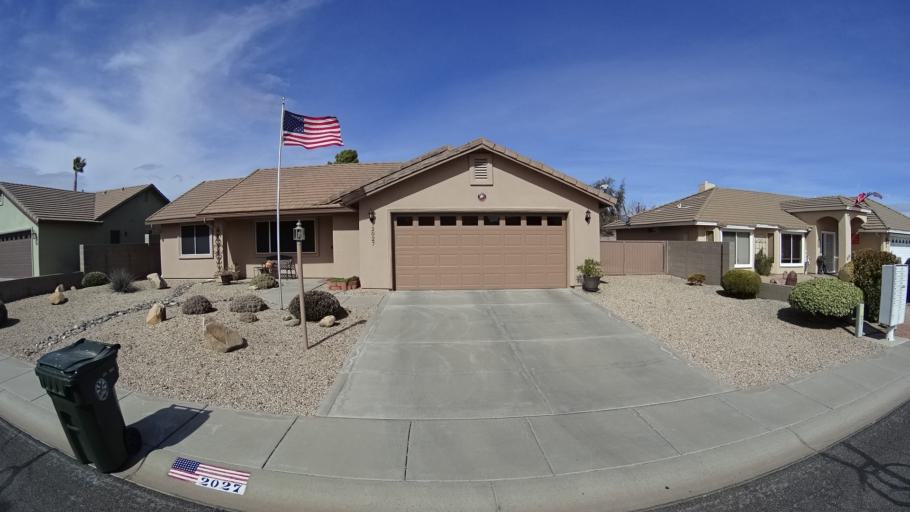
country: US
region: Arizona
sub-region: Mohave County
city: New Kingman-Butler
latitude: 35.2354
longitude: -114.0306
